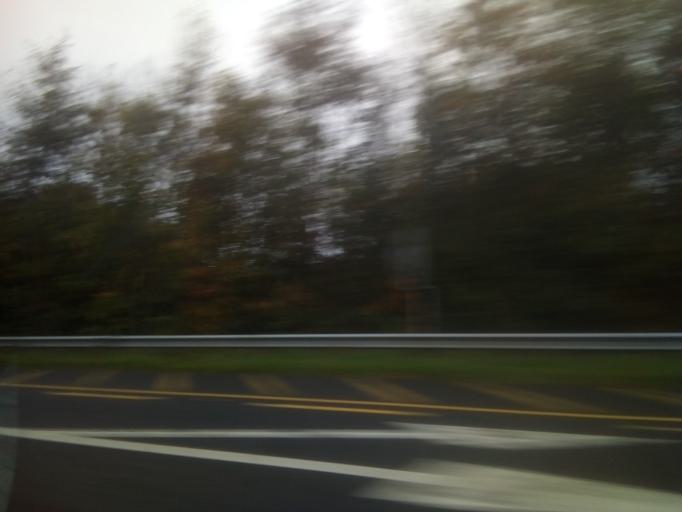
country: IE
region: Leinster
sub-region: An Iarmhi
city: An Muileann gCearr
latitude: 53.5968
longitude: -7.3840
